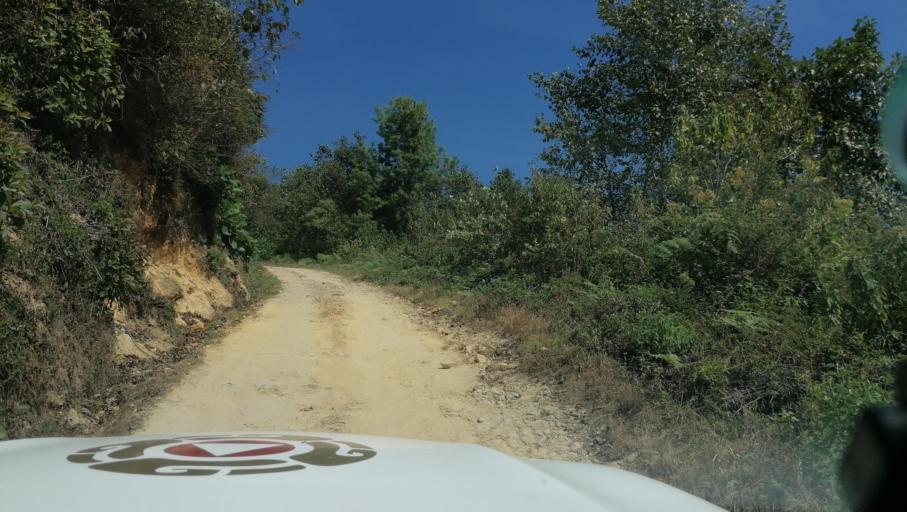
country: GT
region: San Marcos
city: Tacana
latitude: 15.2093
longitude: -92.2155
